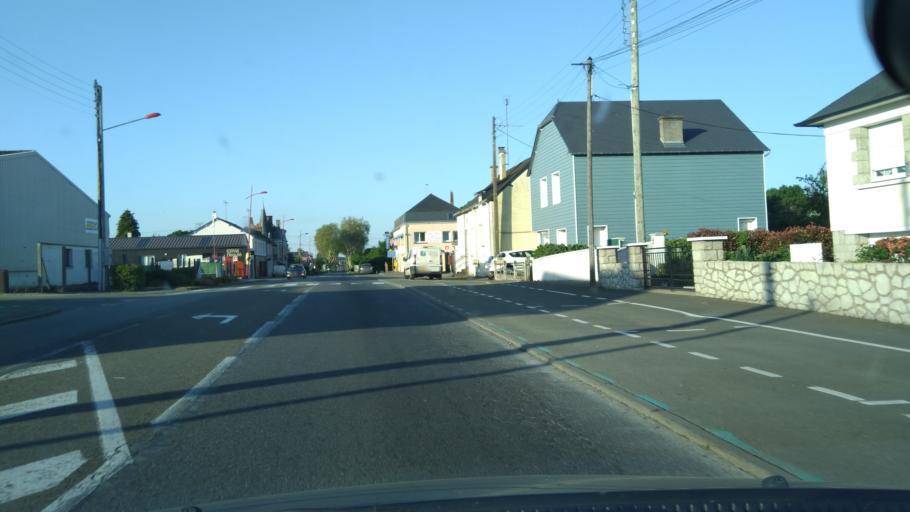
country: FR
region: Pays de la Loire
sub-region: Departement de la Mayenne
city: Cosse-le-Vivien
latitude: 47.9510
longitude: -0.9060
